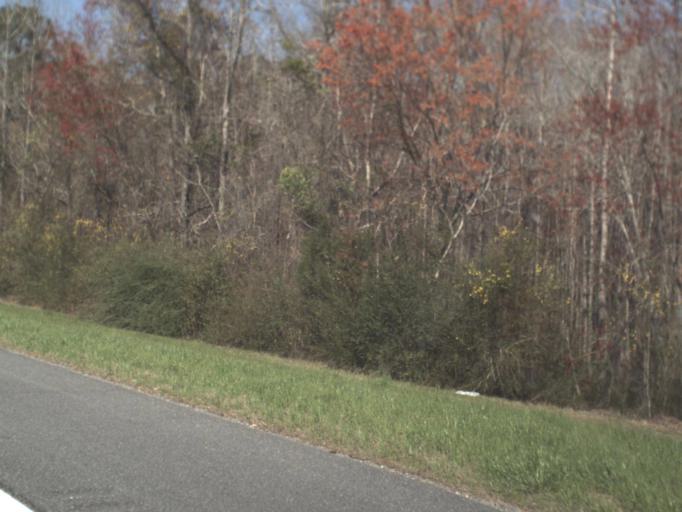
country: US
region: Florida
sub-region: Jackson County
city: Marianna
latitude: 30.7551
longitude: -85.3693
